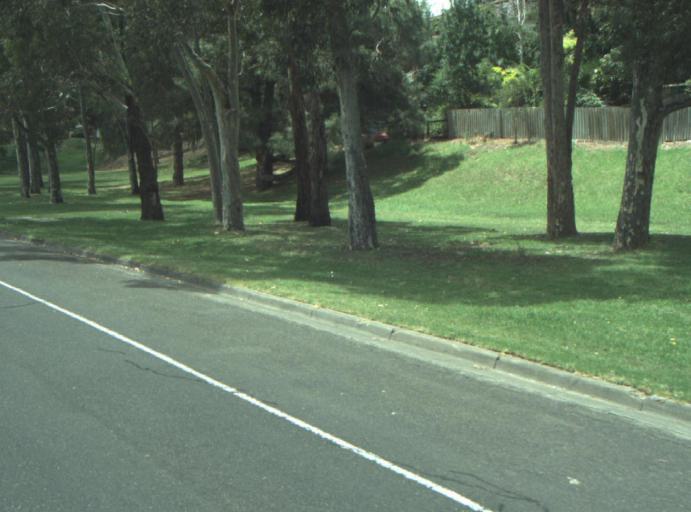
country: AU
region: Victoria
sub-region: Greater Geelong
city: Wandana Heights
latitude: -38.1745
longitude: 144.3231
